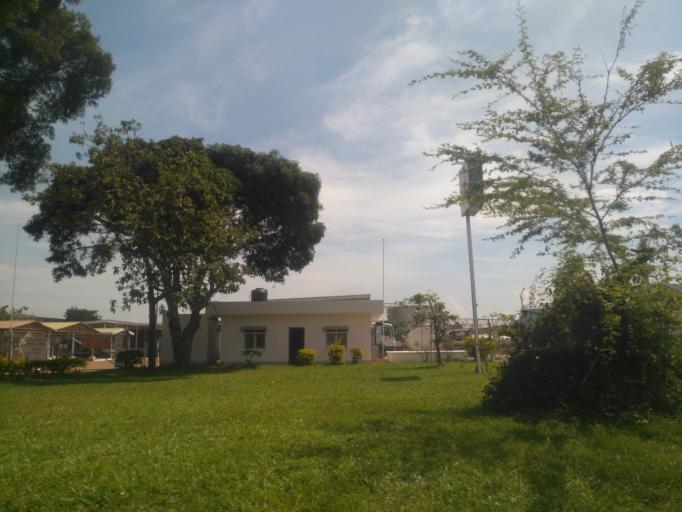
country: UG
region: Central Region
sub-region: Wakiso District
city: Entebbe
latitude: 0.0428
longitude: 32.4434
